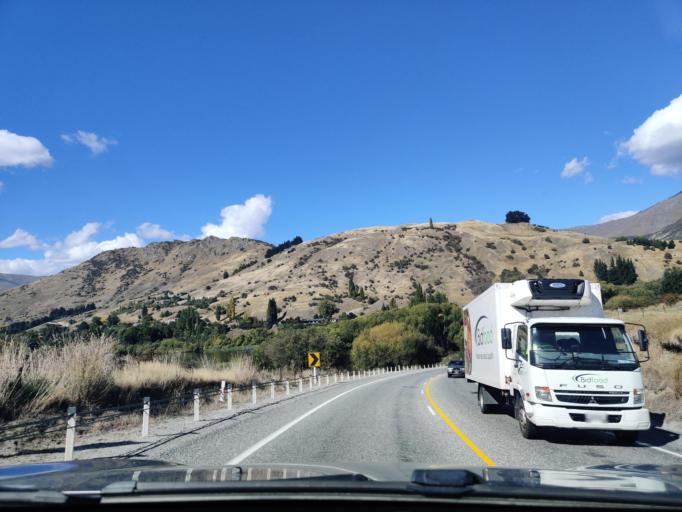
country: NZ
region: Otago
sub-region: Queenstown-Lakes District
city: Arrowtown
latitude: -44.9940
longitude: 168.7978
